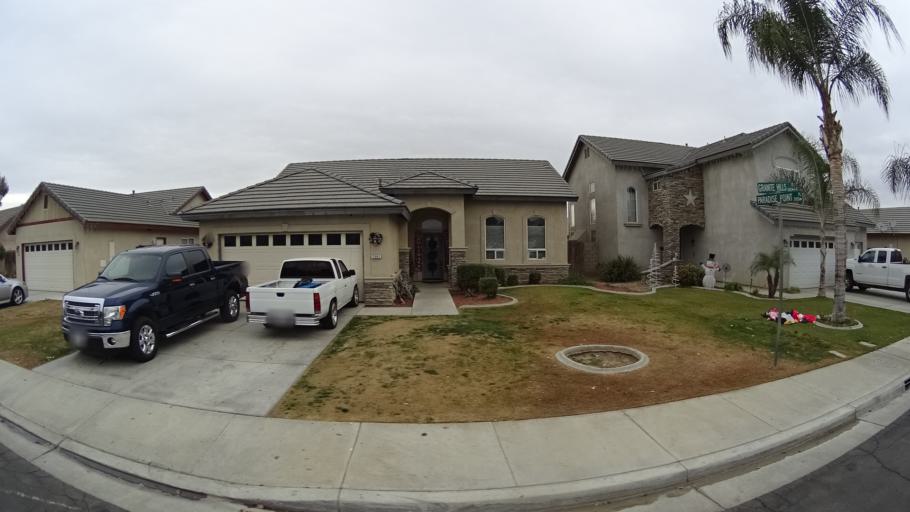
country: US
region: California
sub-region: Kern County
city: Greenfield
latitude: 35.2871
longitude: -119.0353
